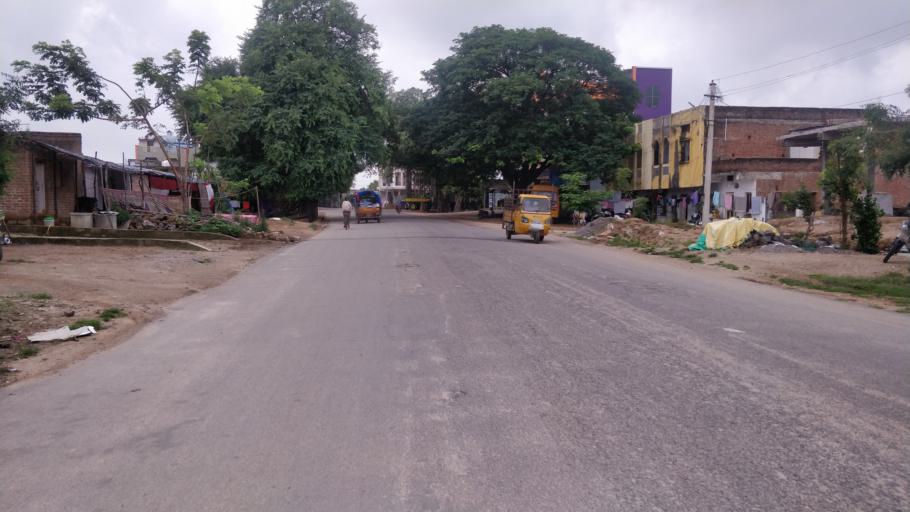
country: IN
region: Telangana
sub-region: Medak
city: Narsingi
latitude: 18.1848
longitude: 78.3977
